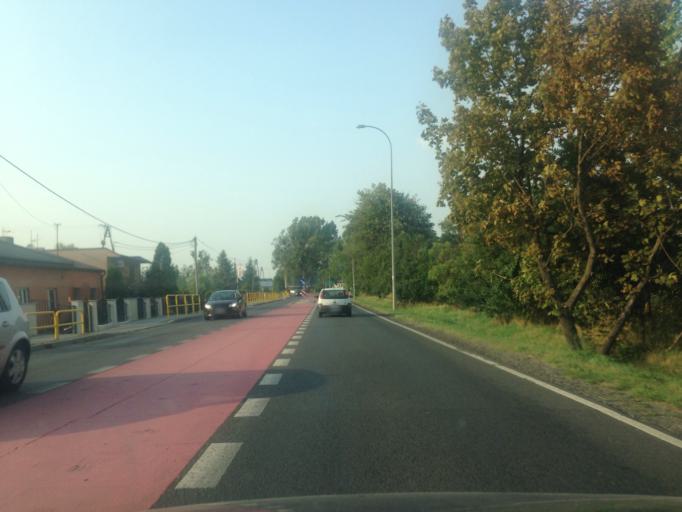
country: PL
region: Kujawsko-Pomorskie
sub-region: Powiat wloclawski
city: Fabianki
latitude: 52.7215
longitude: 19.1106
